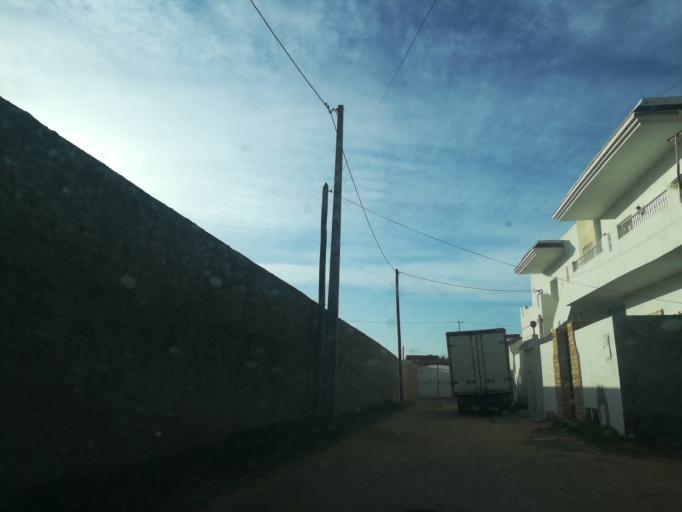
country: TN
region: Safaqis
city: Al Qarmadah
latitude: 34.8139
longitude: 10.7516
